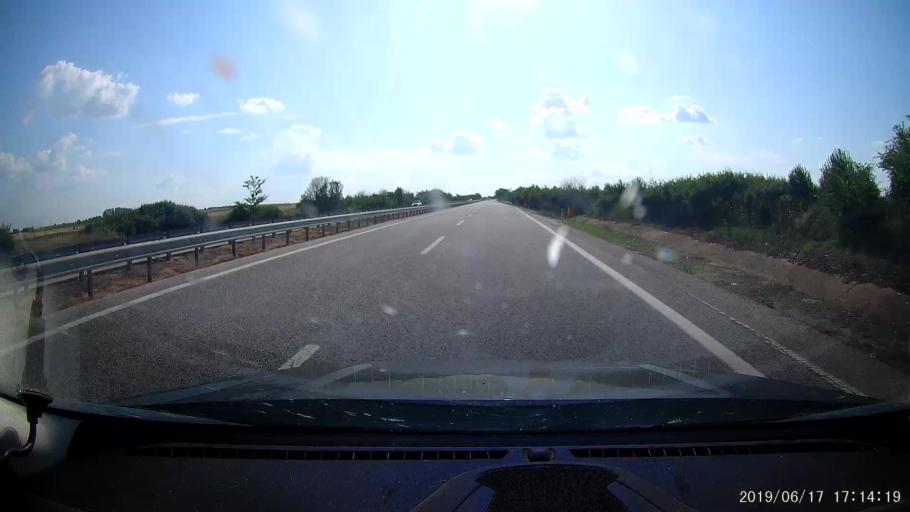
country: TR
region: Edirne
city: Edirne
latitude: 41.6997
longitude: 26.5215
